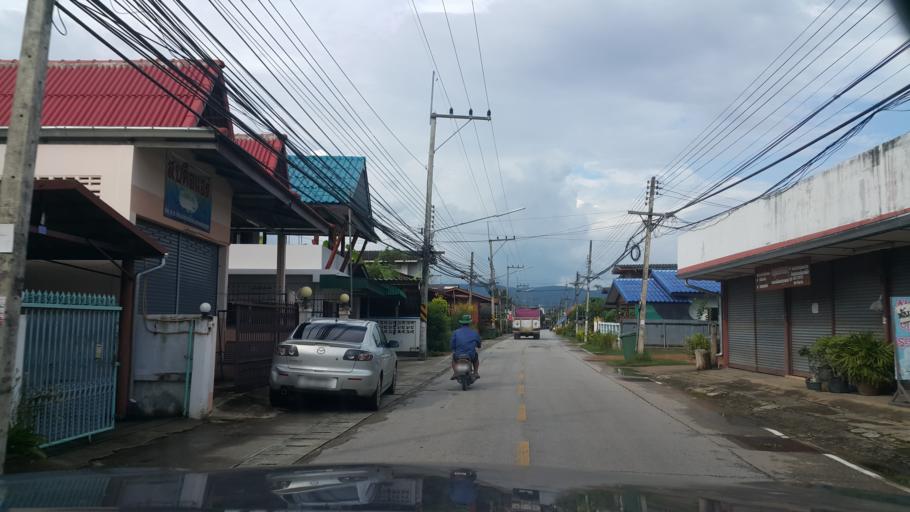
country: TH
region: Lampang
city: Thoen
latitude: 17.6181
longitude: 99.2222
